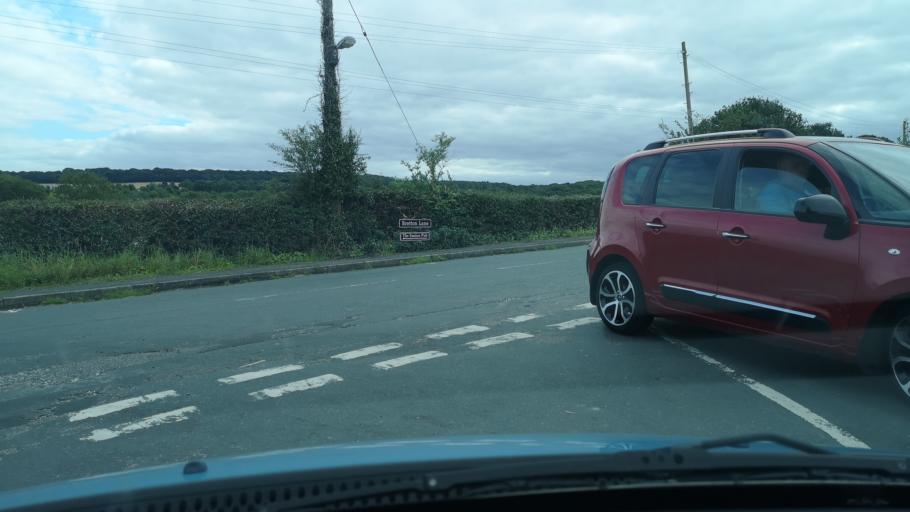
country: GB
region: England
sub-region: City and Borough of Wakefield
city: Crigglestone
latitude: 53.6344
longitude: -1.5457
